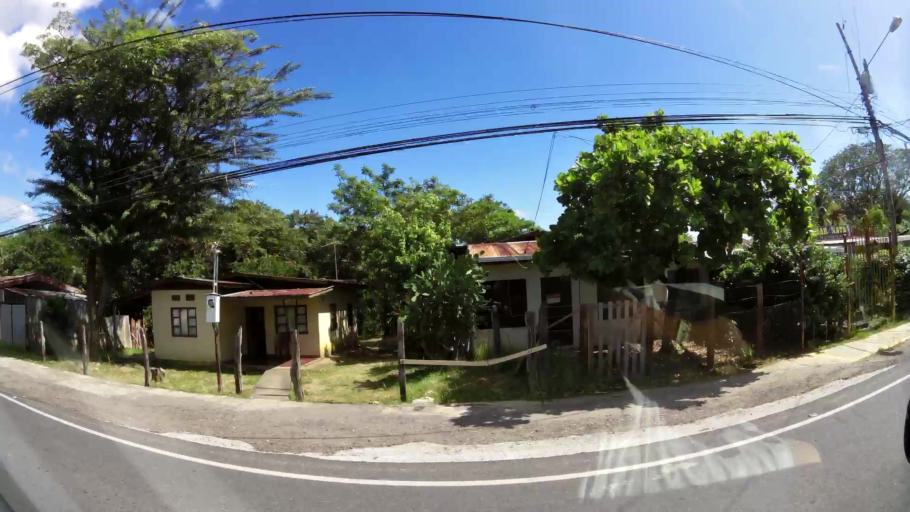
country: CR
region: Guanacaste
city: Bagaces
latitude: 10.5319
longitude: -85.2557
